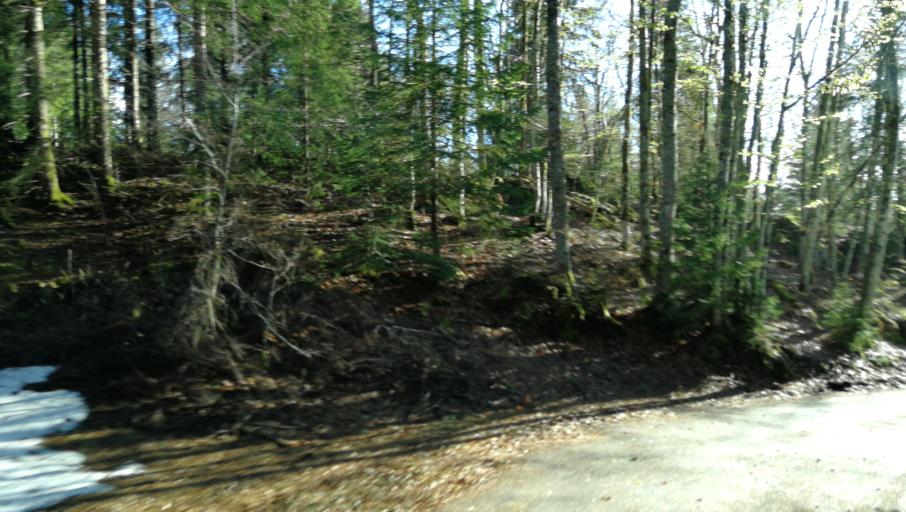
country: FR
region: Rhone-Alpes
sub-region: Departement de l'Ain
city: Chatillon-en-Michaille
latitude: 46.2634
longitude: 5.7985
